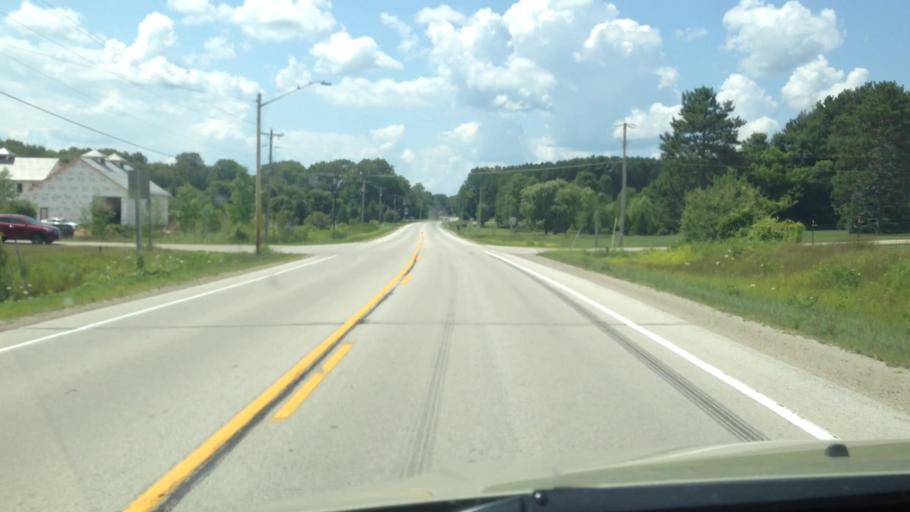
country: US
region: Wisconsin
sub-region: Brown County
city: Suamico
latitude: 44.6463
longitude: -88.0997
